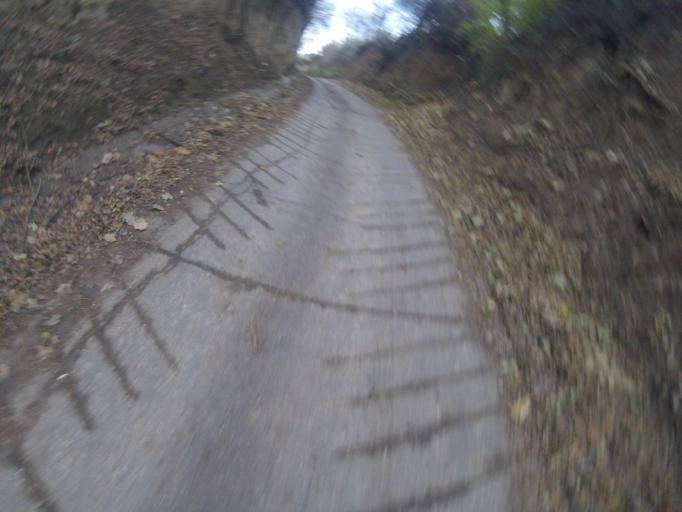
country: HU
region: Tolna
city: Szekszard
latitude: 46.3414
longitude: 18.6918
